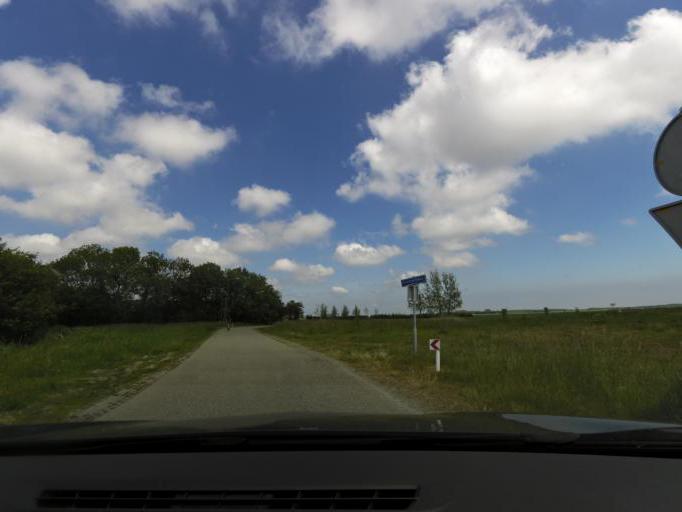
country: NL
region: Zeeland
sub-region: Schouwen-Duiveland
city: Haamstede
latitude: 51.6993
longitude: 3.7514
